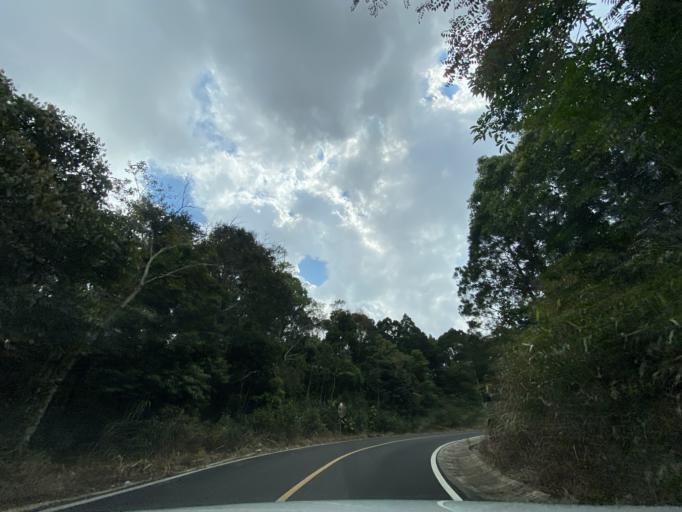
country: CN
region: Hainan
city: Diaoluoshan
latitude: 18.7214
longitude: 109.8720
